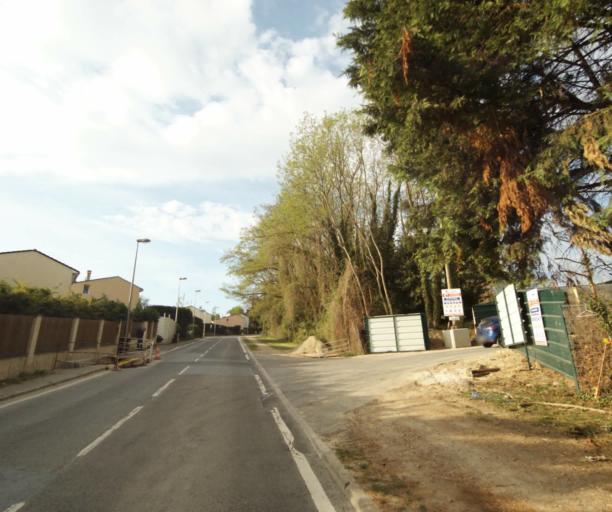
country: FR
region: Ile-de-France
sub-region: Departement de Seine-et-Marne
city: Torcy
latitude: 48.8580
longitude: 2.6559
